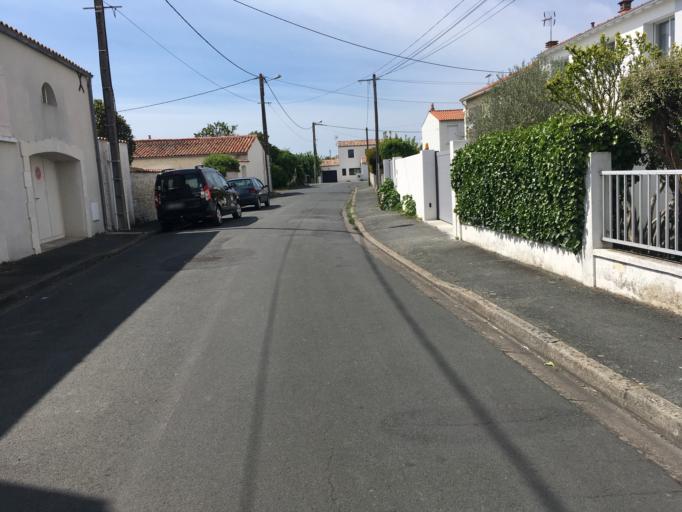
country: FR
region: Poitou-Charentes
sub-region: Departement de la Charente-Maritime
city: Aytre
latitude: 46.1350
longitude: -1.1150
